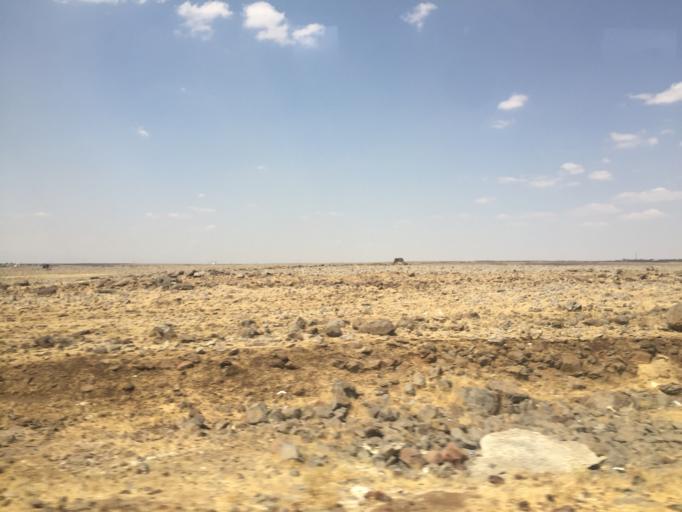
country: TR
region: Sanliurfa
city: Siverek
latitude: 37.7793
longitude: 39.4679
